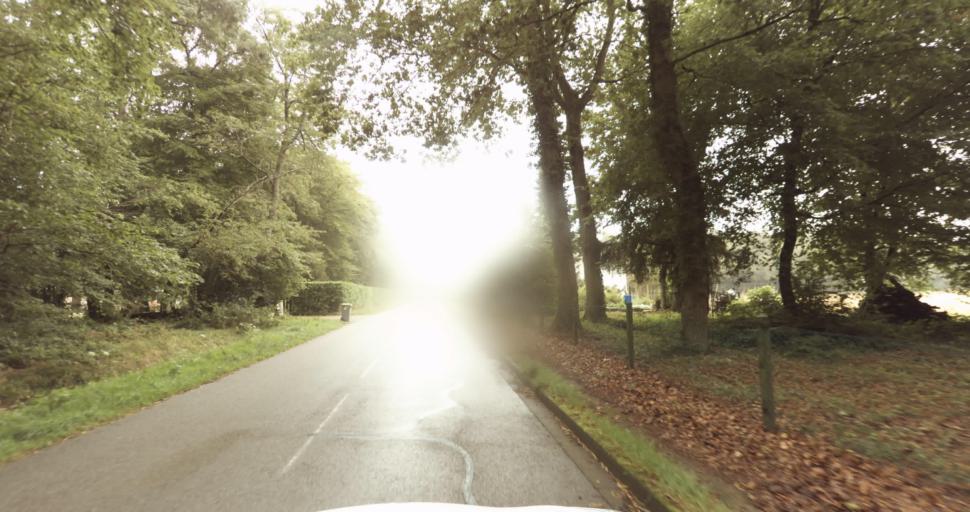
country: FR
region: Haute-Normandie
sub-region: Departement de l'Eure
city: Normanville
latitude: 49.1014
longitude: 1.1431
